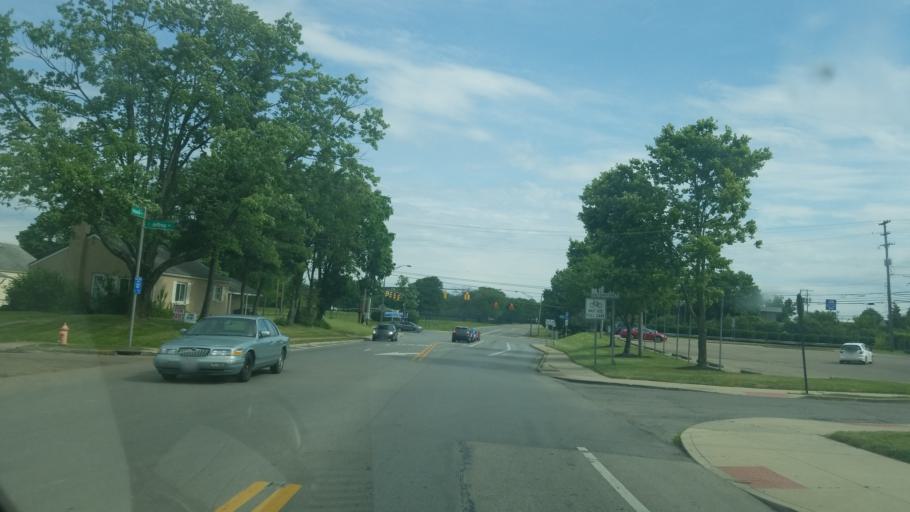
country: US
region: Ohio
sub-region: Franklin County
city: Worthington
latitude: 40.0606
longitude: -83.0010
